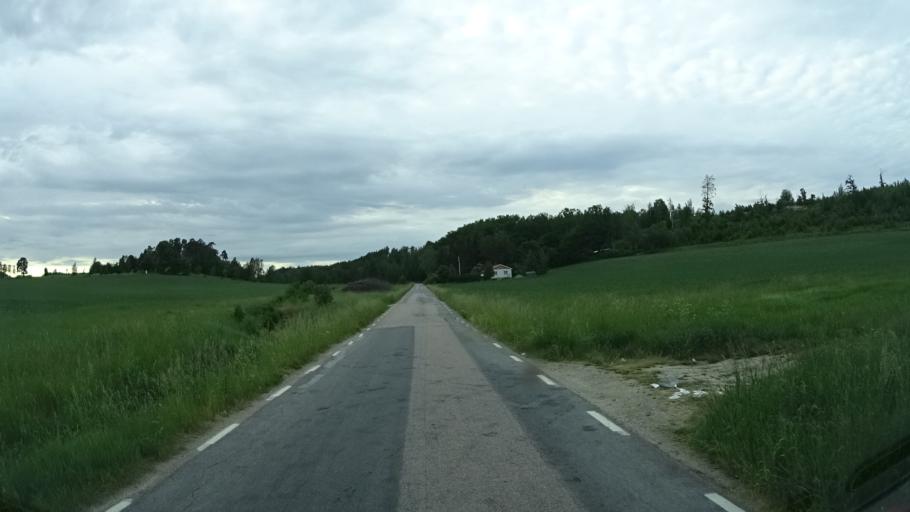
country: SE
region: Soedermanland
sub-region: Nykopings Kommun
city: Stigtomta
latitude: 58.7515
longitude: 16.7247
